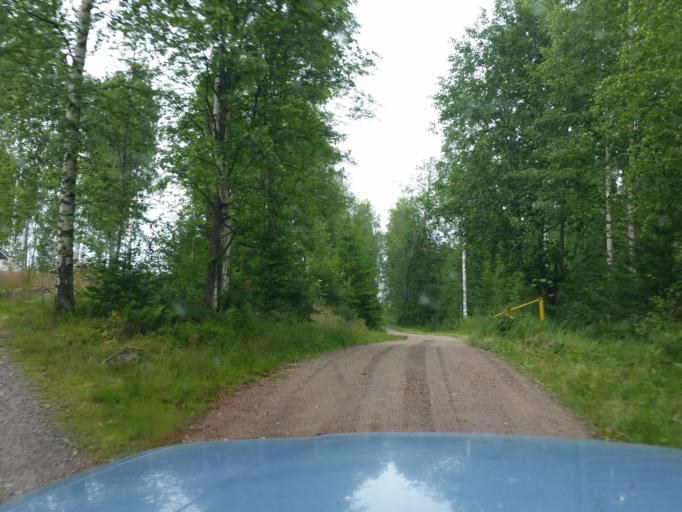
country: FI
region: Uusimaa
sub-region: Helsinki
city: Kaerkoelae
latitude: 60.5719
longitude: 24.0035
